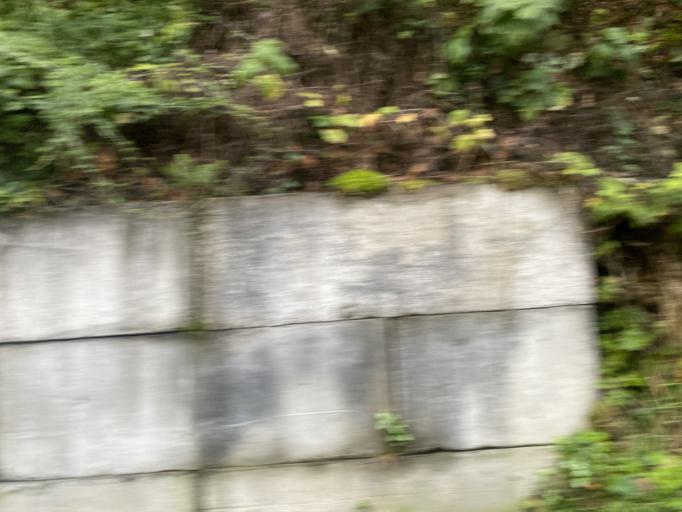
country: US
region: Washington
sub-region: Island County
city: Camano
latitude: 48.0952
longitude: -122.4990
